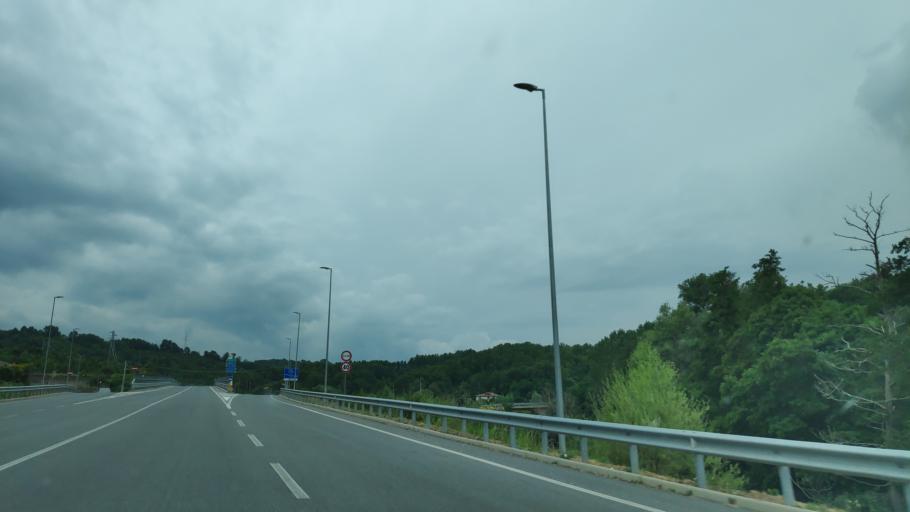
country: IT
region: Calabria
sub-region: Provincia di Catanzaro
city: Cardinale
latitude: 38.6489
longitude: 16.3801
